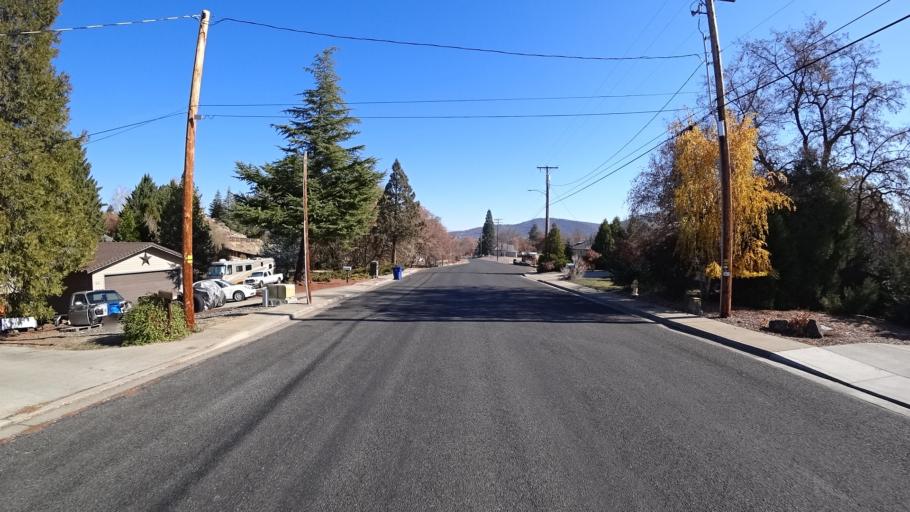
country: US
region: California
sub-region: Siskiyou County
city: Yreka
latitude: 41.7316
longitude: -122.6488
